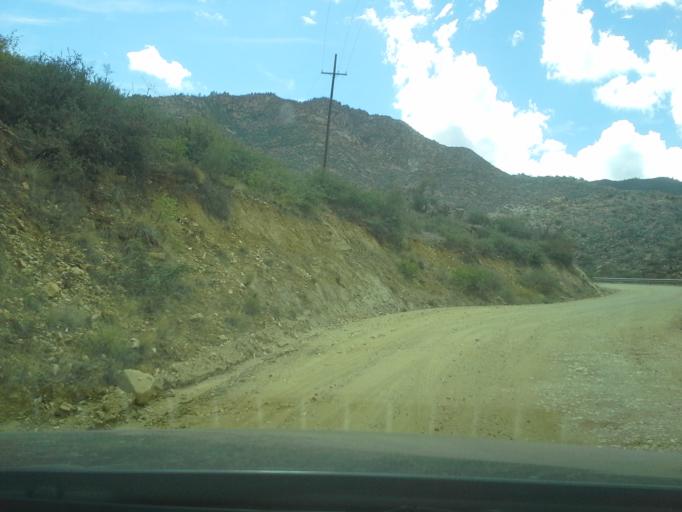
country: US
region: Arizona
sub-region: Yavapai County
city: Mayer
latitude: 34.2563
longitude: -112.2964
